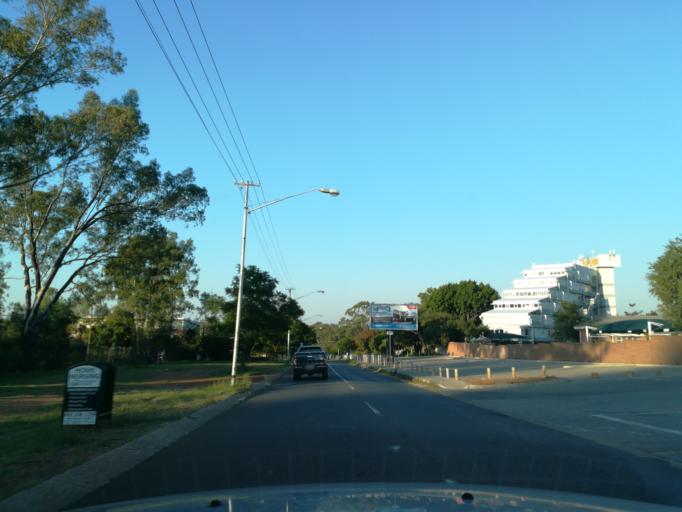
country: ZA
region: Gauteng
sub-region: City of Tshwane Metropolitan Municipality
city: Pretoria
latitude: -25.7698
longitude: 28.2162
